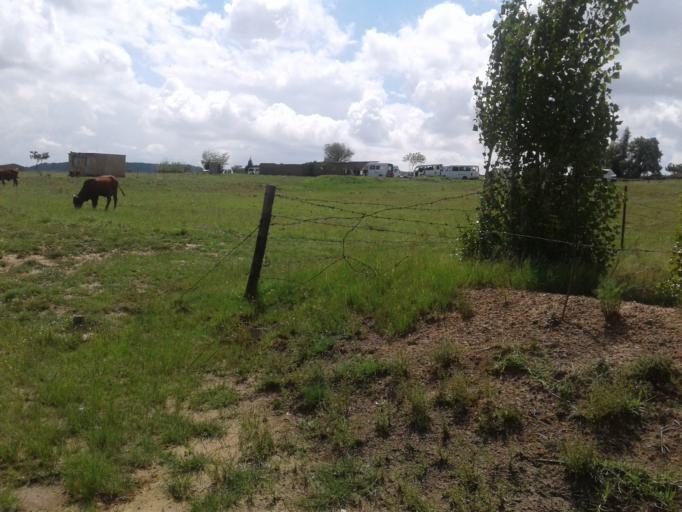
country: LS
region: Mafeteng
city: Mafeteng
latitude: -29.7485
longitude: 27.1123
